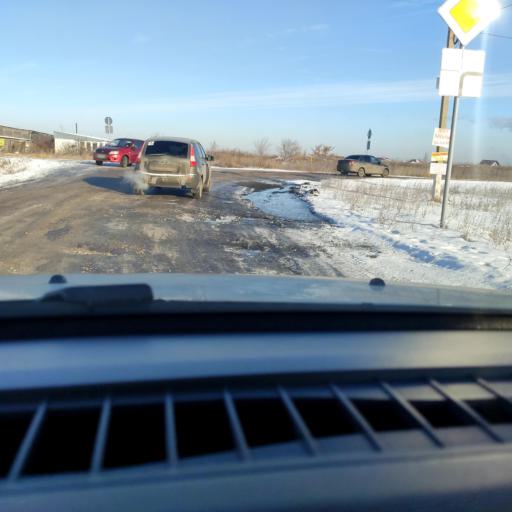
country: RU
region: Samara
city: Podstepki
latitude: 53.5227
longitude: 49.1460
